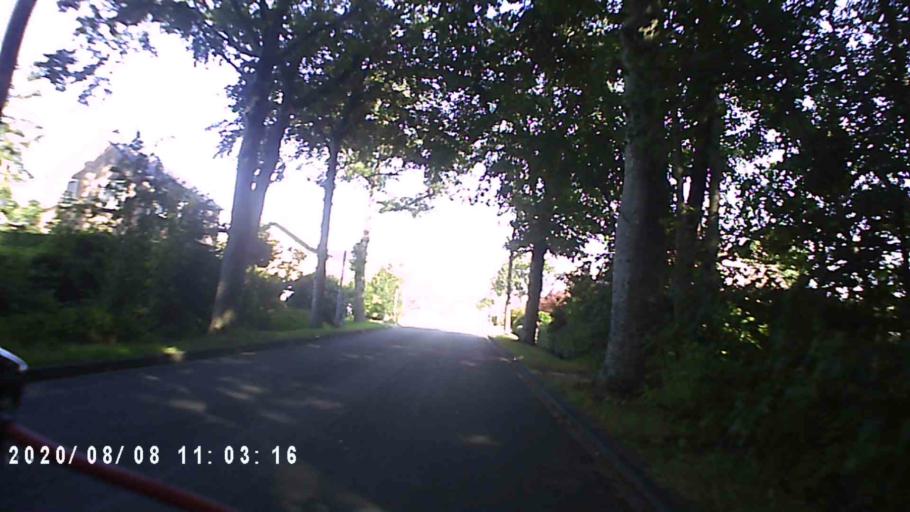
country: NL
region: Groningen
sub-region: Gemeente Leek
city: Leek
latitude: 53.1579
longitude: 6.3951
